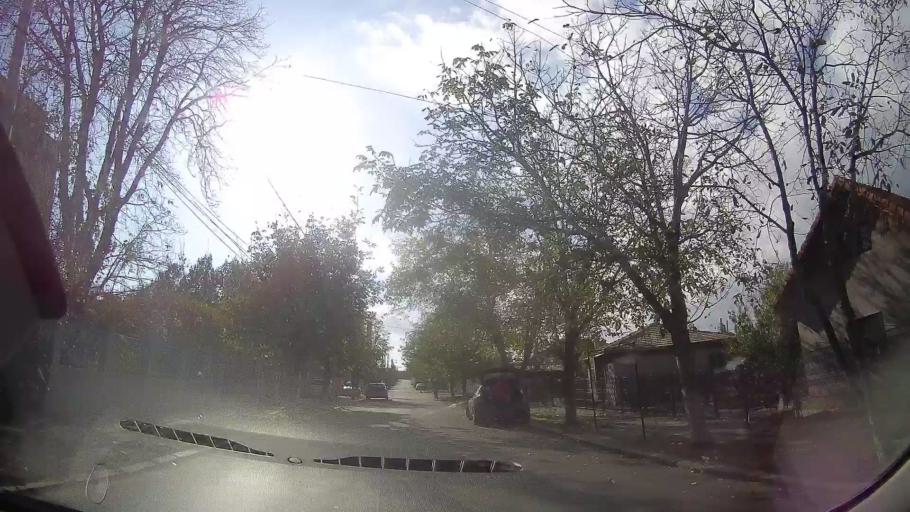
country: RO
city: Eforie Sud
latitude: 44.0202
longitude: 28.6486
